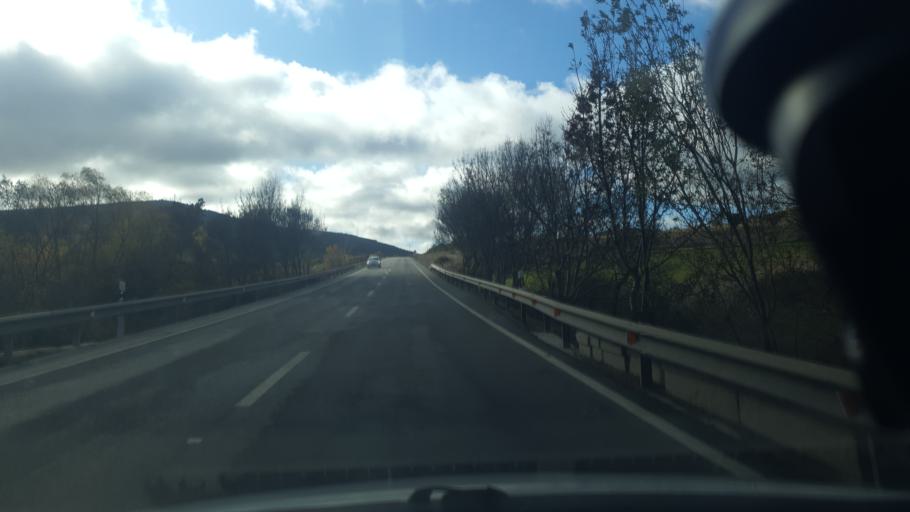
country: ES
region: Castille and Leon
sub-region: Provincia de Segovia
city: Villacastin
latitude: 40.7468
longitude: -4.4617
